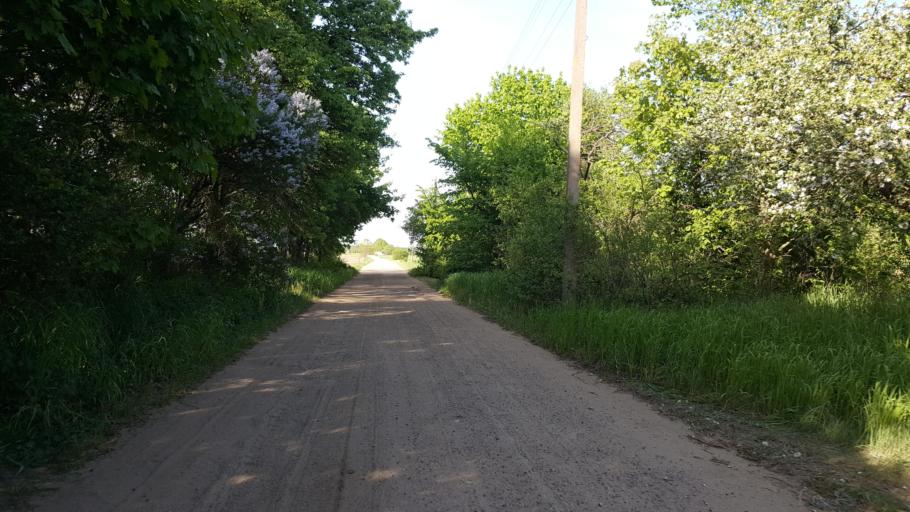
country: BY
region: Brest
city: Kamyanyets
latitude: 52.3627
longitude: 23.8696
